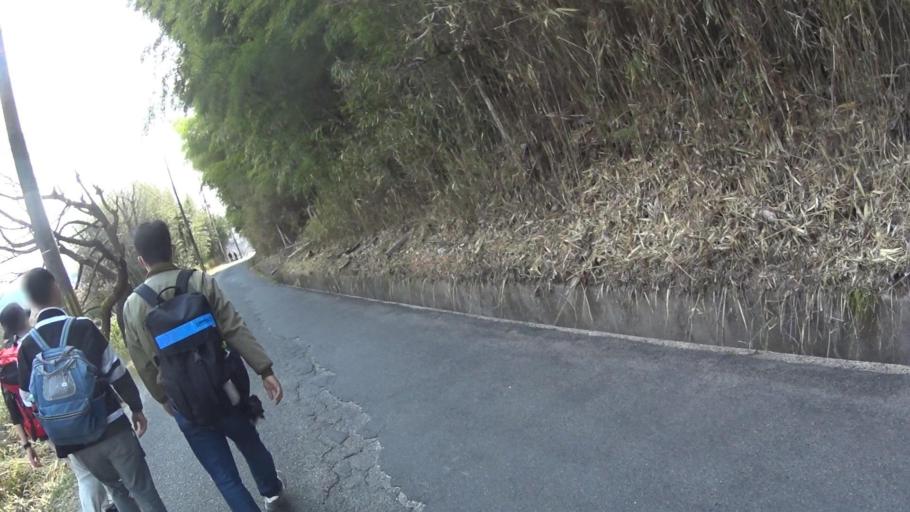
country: JP
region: Nara
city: Nara-shi
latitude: 34.7245
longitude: 135.8394
